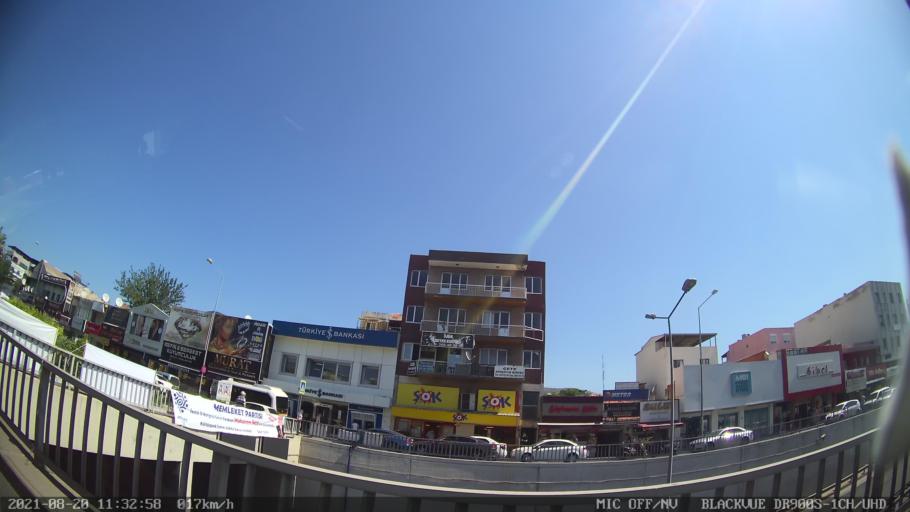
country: TR
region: Izmir
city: Karsiyaka
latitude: 38.4935
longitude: 27.0627
